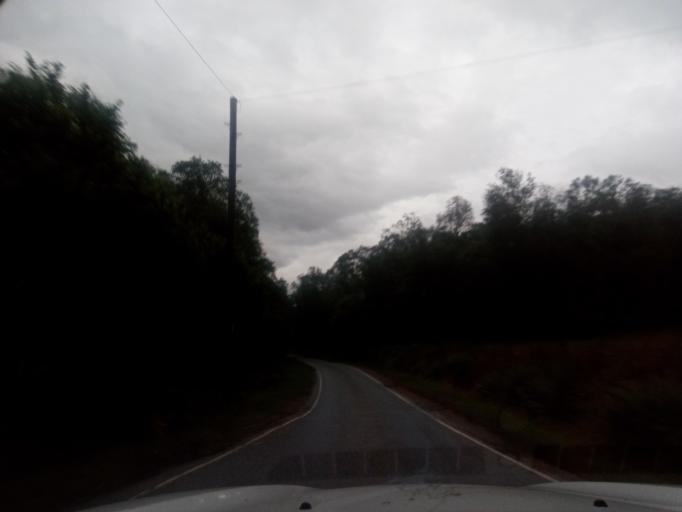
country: GB
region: Scotland
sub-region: Highland
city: Fort William
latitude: 56.8458
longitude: -5.2821
